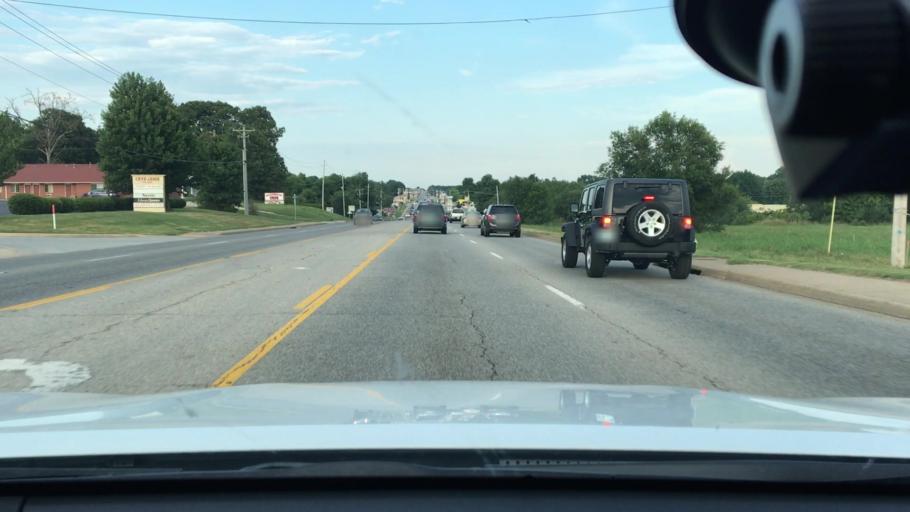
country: US
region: Arkansas
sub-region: Benton County
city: Rogers
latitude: 36.3345
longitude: -94.1657
